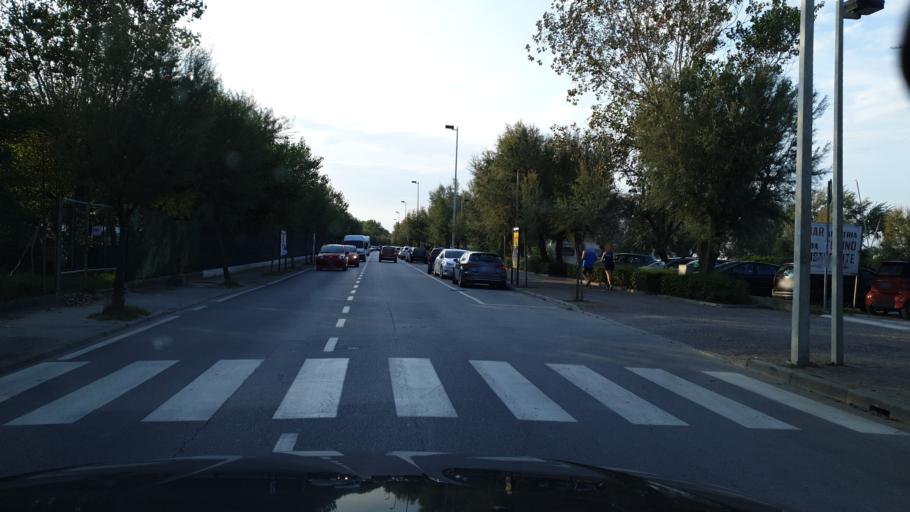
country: IT
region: Emilia-Romagna
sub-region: Provincia di Rimini
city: Misano Adriatico
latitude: 43.9902
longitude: 12.6805
